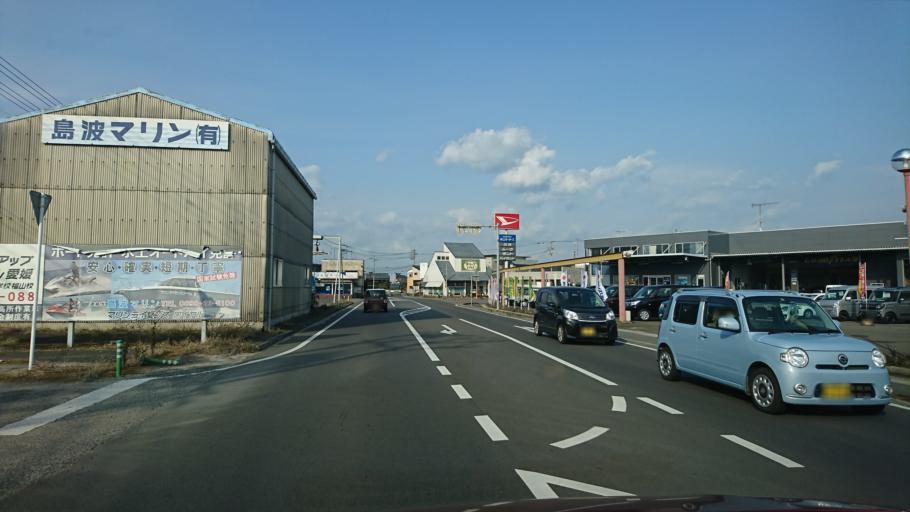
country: JP
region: Ehime
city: Saijo
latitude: 34.0252
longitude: 133.0381
